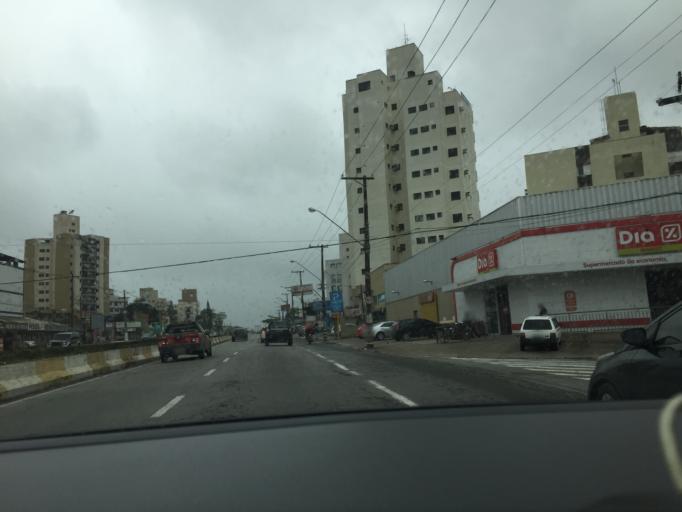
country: BR
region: Sao Paulo
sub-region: Guaruja
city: Guaruja
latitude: -23.9811
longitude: -46.2270
